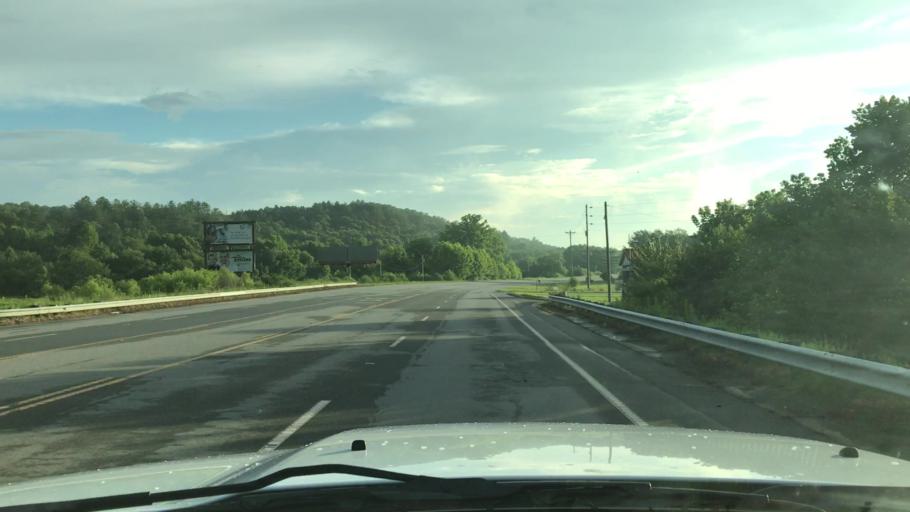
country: US
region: North Carolina
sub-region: Cherokee County
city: Murphy
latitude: 34.9906
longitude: -84.1661
